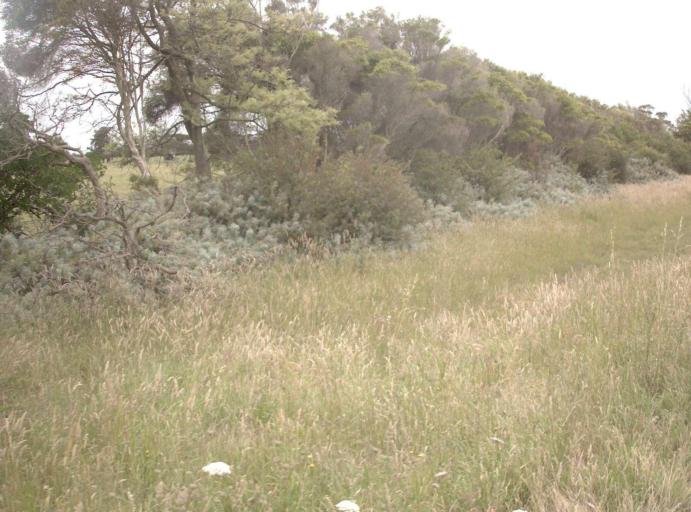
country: AU
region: Victoria
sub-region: Bass Coast
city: North Wonthaggi
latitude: -38.5764
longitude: 145.6324
